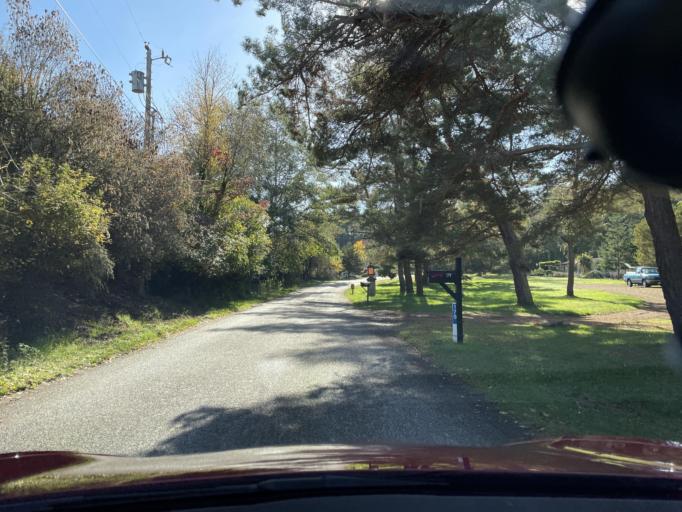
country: US
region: Washington
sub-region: San Juan County
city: Friday Harbor
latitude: 48.4605
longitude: -122.9634
